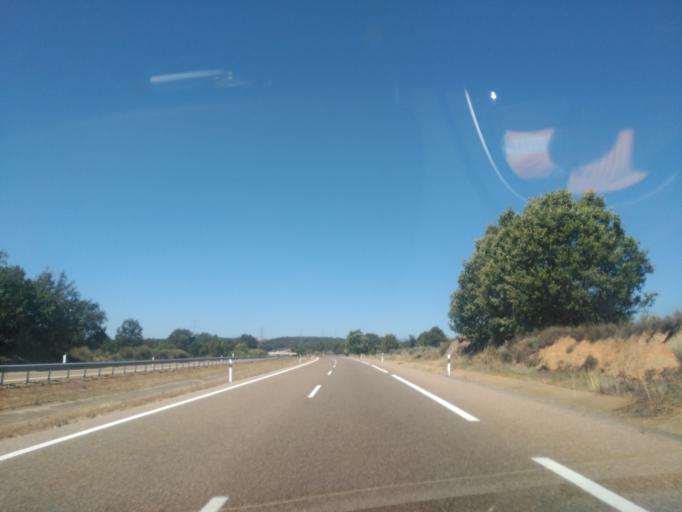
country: ES
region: Castille and Leon
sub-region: Provincia de Zamora
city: Mombuey
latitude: 42.0182
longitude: -6.3217
